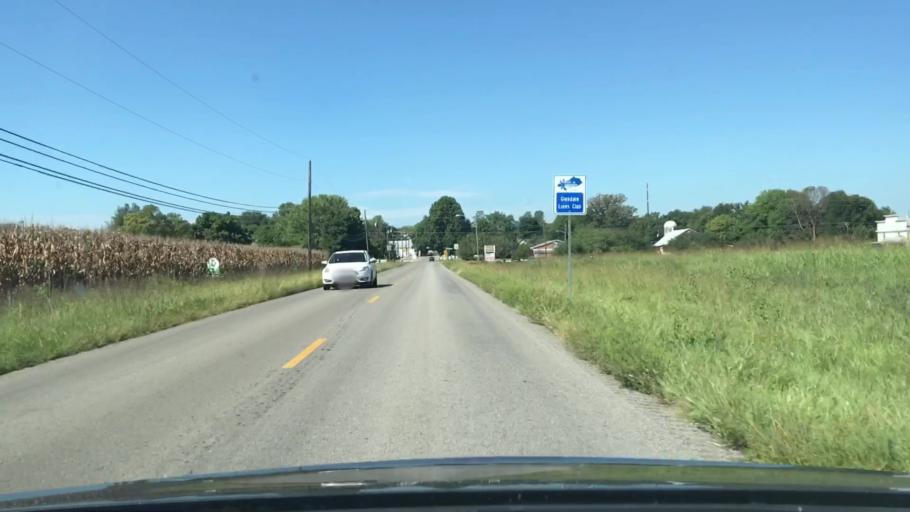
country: US
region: Kentucky
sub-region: Hardin County
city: Elizabethtown
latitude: 37.6016
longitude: -85.9003
